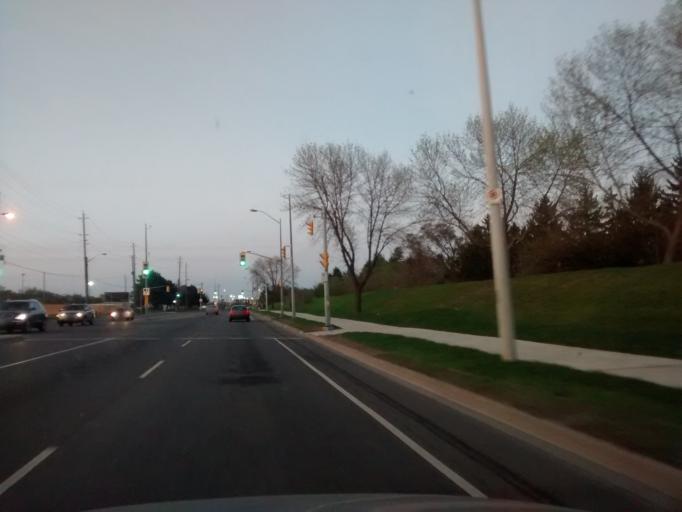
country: CA
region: Ontario
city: Burlington
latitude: 43.3380
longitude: -79.8103
